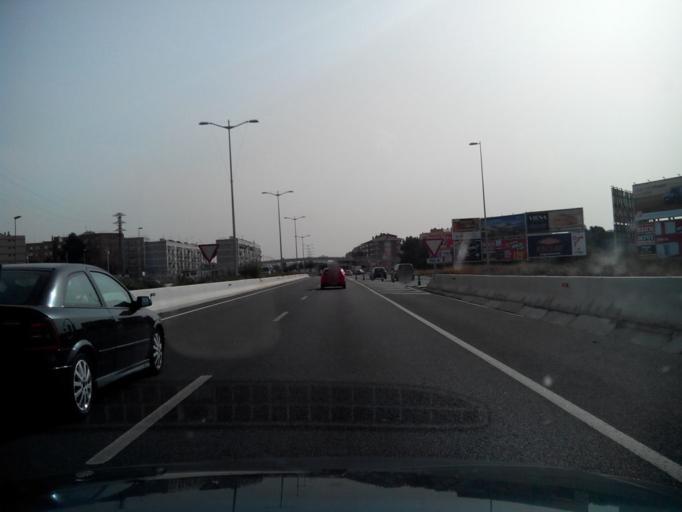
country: ES
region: Catalonia
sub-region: Provincia de Tarragona
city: Constanti
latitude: 41.1259
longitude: 1.2083
